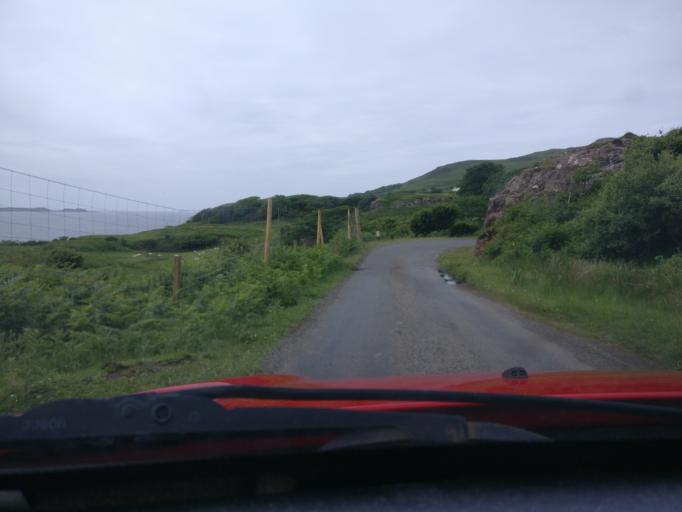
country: GB
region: Scotland
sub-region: Argyll and Bute
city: Isle Of Mull
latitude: 56.5310
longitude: -6.2313
